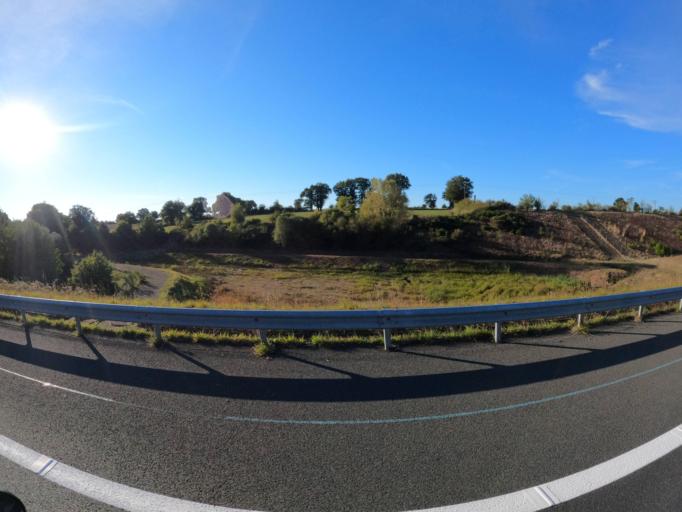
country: FR
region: Pays de la Loire
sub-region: Departement de Maine-et-Loire
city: Chemille-Melay
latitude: 47.2252
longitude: -0.7576
